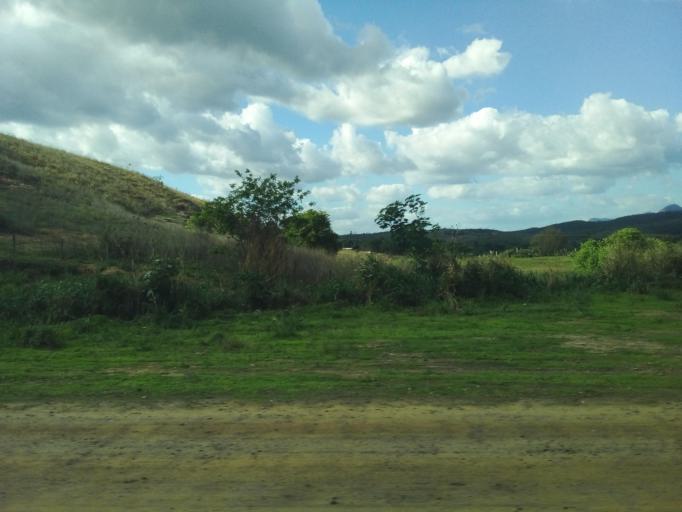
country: BR
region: Minas Gerais
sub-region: Conselheiro Pena
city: Conselheiro Pena
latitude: -18.9832
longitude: -41.6117
